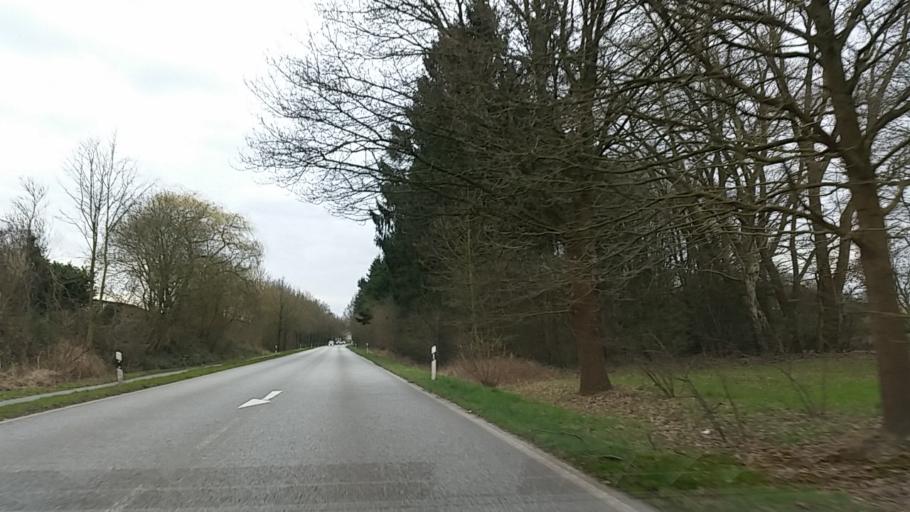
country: DE
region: Schleswig-Holstein
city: Braak
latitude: 53.6145
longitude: 10.2409
